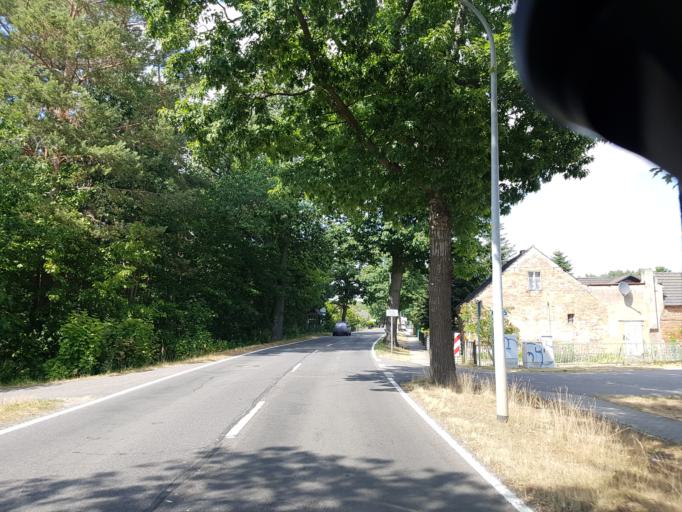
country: DE
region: Brandenburg
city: Kolkwitz
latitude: 51.7419
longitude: 14.2600
